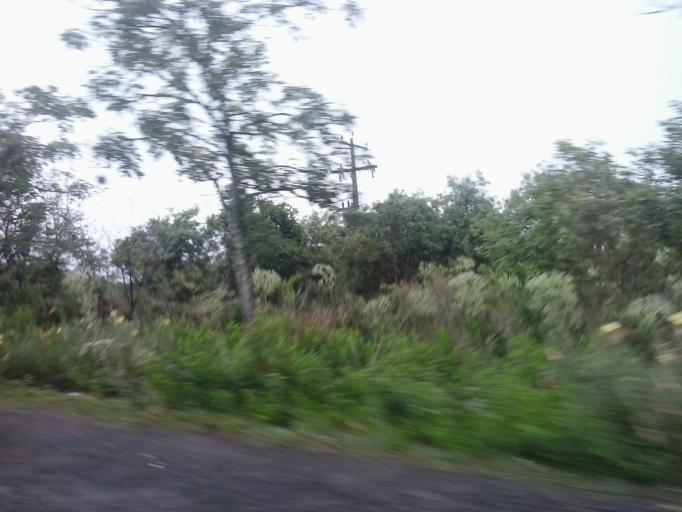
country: BR
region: Rio Grande do Sul
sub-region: Candelaria
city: Candelaria
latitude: -29.7329
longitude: -53.1817
